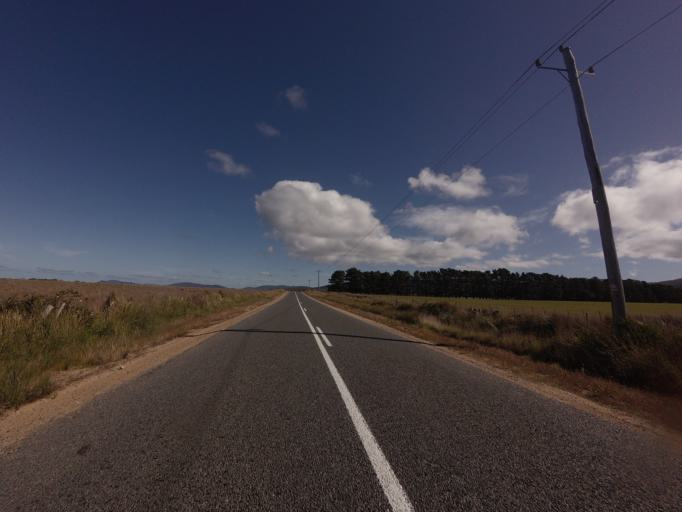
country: AU
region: Tasmania
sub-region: Break O'Day
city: St Helens
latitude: -41.7537
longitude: 148.2758
